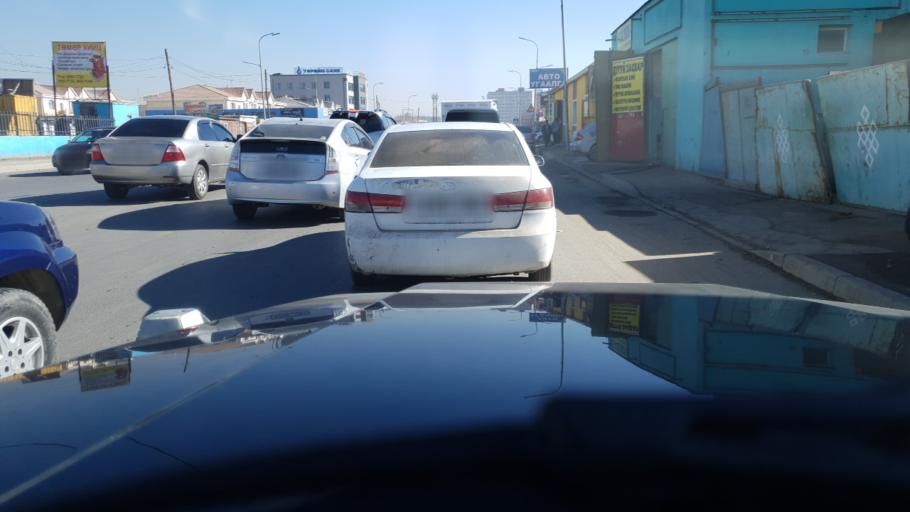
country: MN
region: Ulaanbaatar
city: Ulaanbaatar
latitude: 47.9241
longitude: 106.9692
